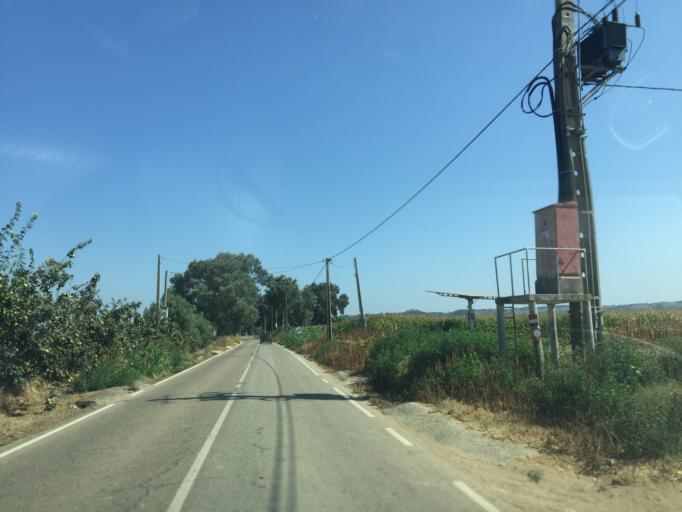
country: PT
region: Santarem
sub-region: Golega
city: Golega
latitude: 39.3336
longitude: -8.4990
